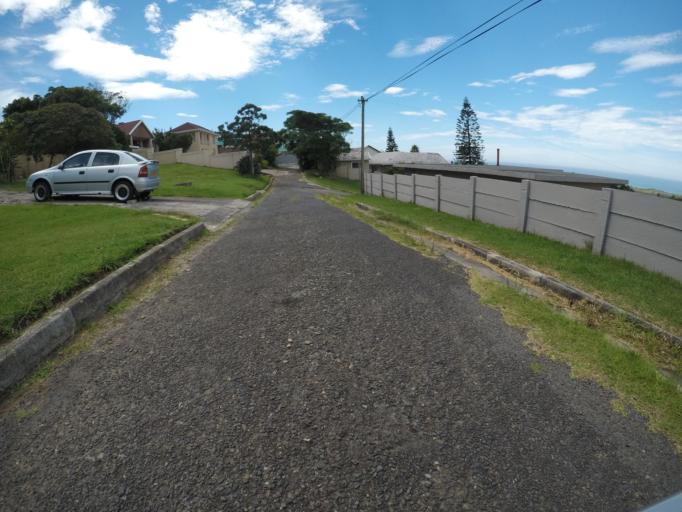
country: ZA
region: Eastern Cape
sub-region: Buffalo City Metropolitan Municipality
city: East London
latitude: -33.0368
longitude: 27.8587
